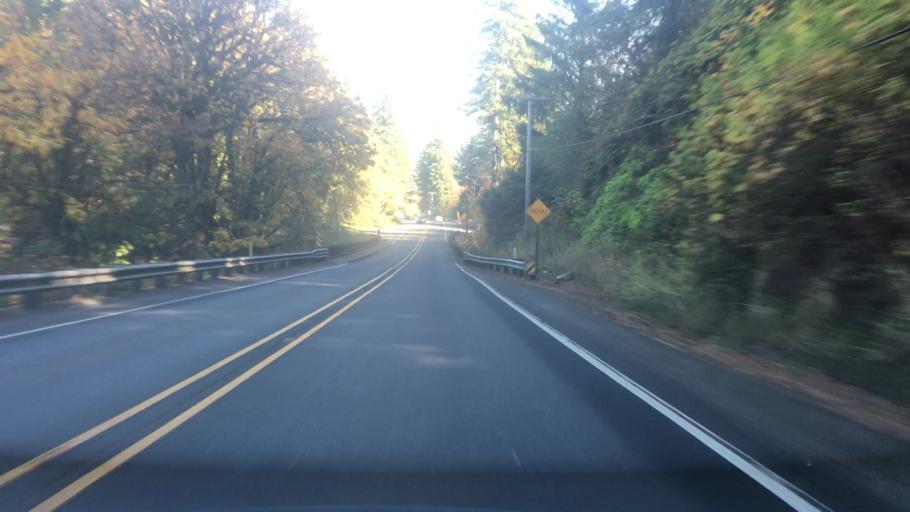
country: US
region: Oregon
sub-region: Lincoln County
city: Rose Lodge
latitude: 45.0188
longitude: -123.8678
